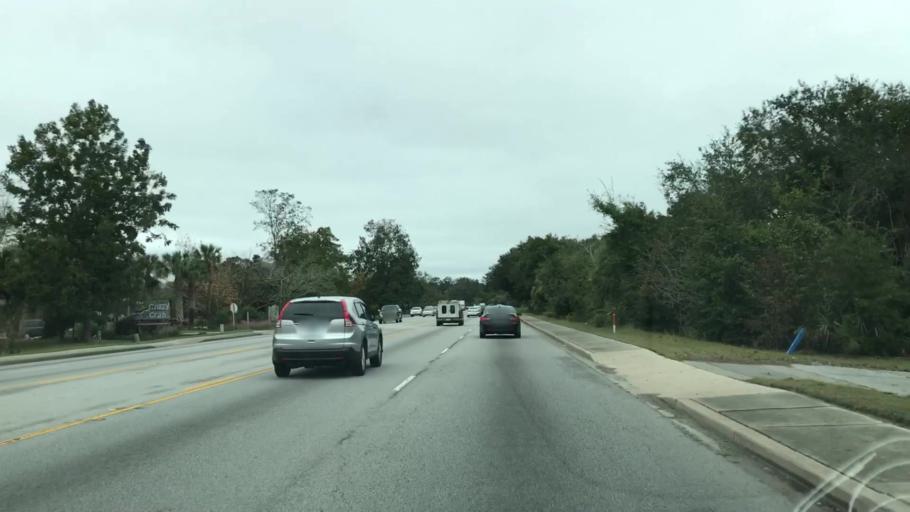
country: US
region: South Carolina
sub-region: Beaufort County
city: Hilton Head Island
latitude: 32.2175
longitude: -80.7577
